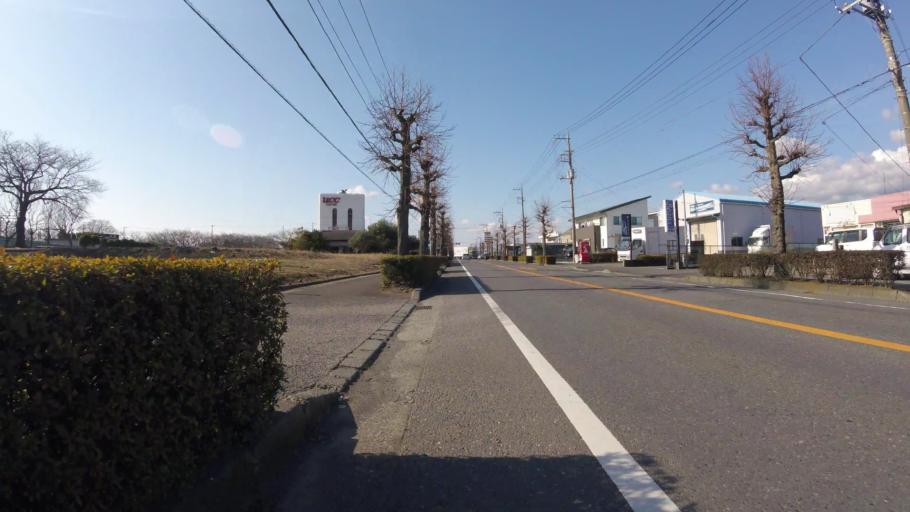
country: JP
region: Shizuoka
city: Fuji
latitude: 35.1563
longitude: 138.7473
